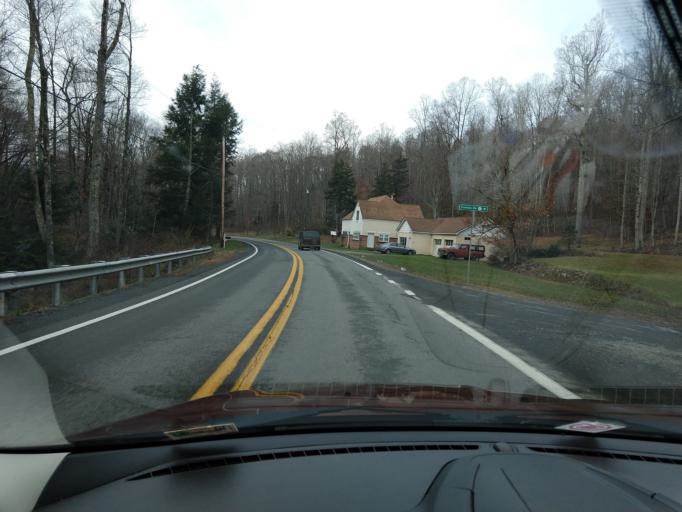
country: US
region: West Virginia
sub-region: Nicholas County
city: Craigsville
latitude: 38.2609
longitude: -80.7400
